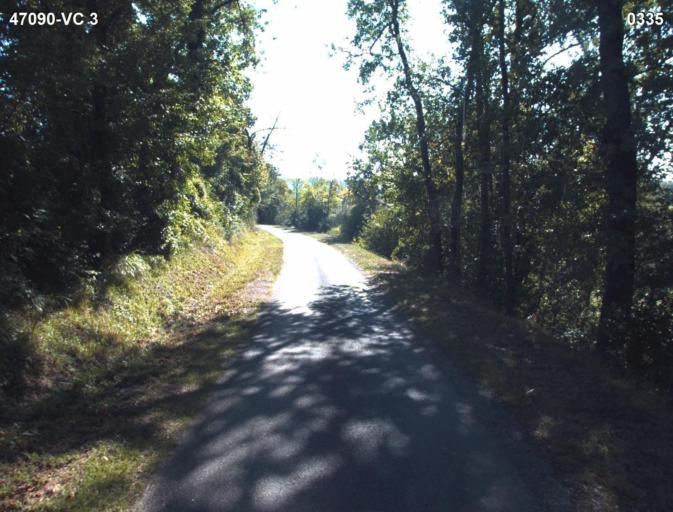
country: FR
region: Aquitaine
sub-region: Departement du Lot-et-Garonne
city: Nerac
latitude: 44.1692
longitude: 0.4156
